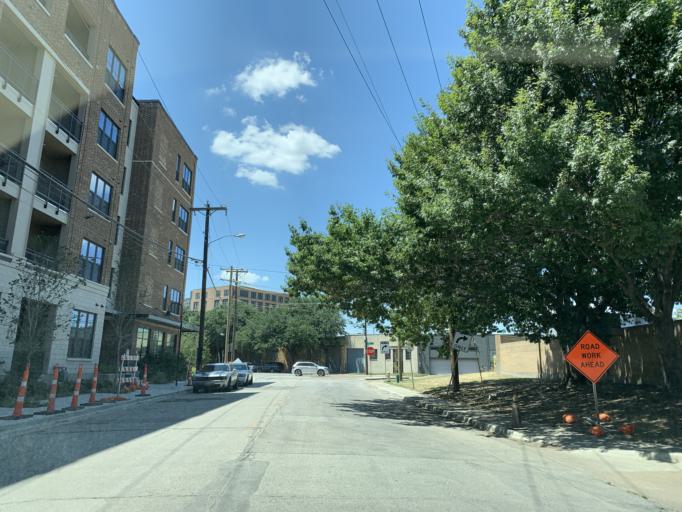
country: US
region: Texas
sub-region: Dallas County
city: Dallas
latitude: 32.7814
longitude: -96.7782
